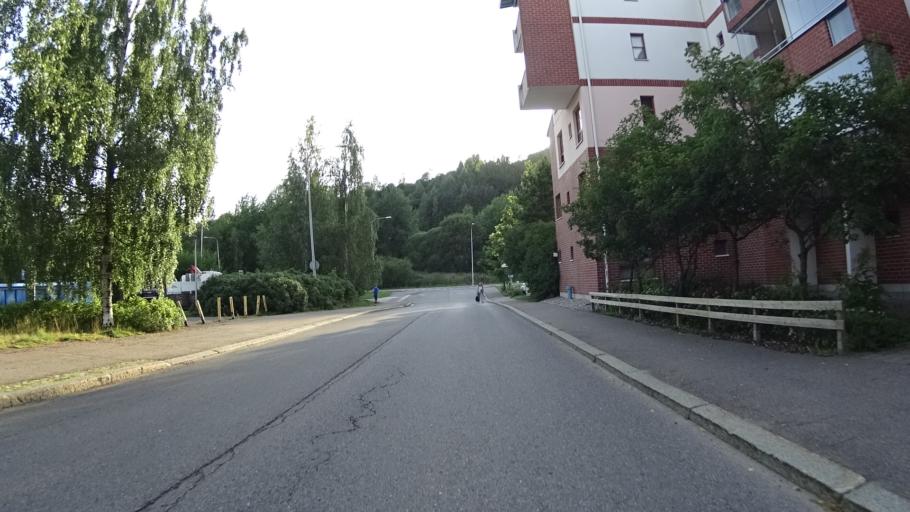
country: FI
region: Uusimaa
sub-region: Helsinki
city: Teekkarikylae
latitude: 60.2514
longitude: 24.8500
